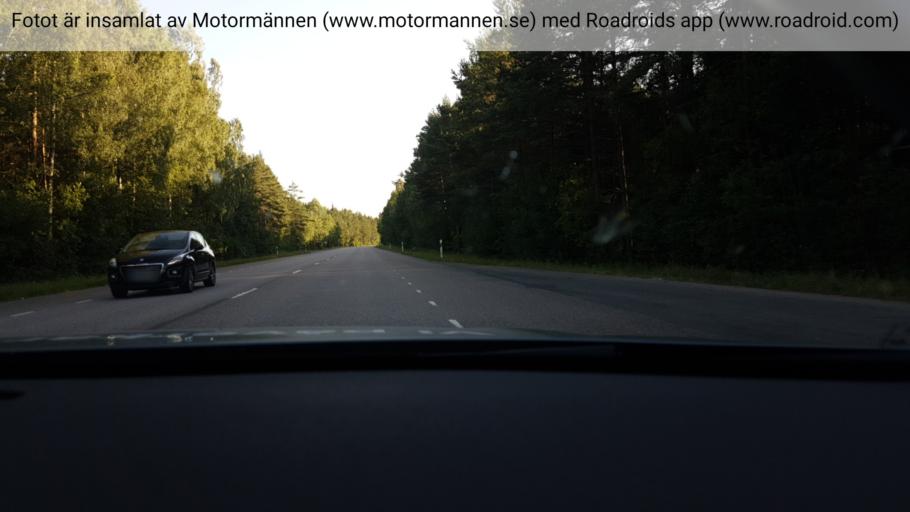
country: SE
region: Vaestra Goetaland
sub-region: Skovde Kommun
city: Stopen
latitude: 58.4299
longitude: 13.9148
